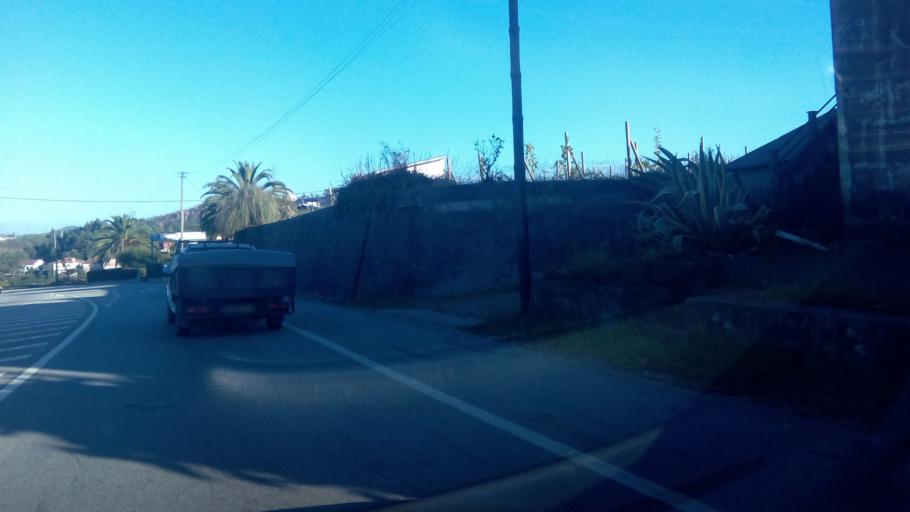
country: PT
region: Porto
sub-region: Paredes
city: Gandra
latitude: 41.1961
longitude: -8.4210
